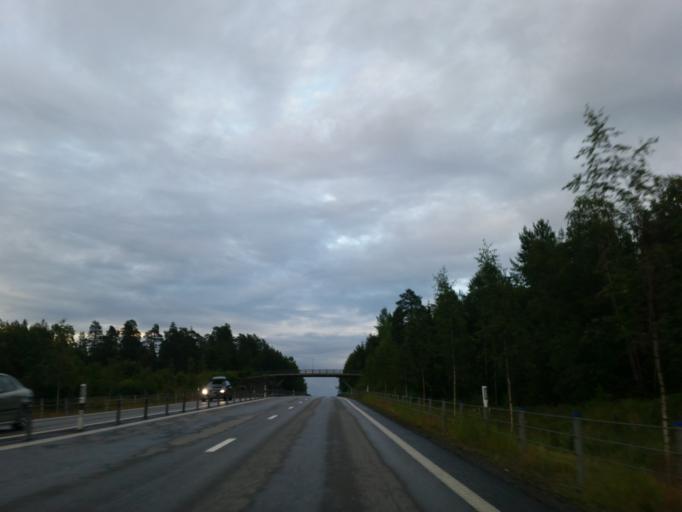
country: SE
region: Vaesterbotten
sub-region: Umea Kommun
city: Ersmark
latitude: 63.8480
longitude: 20.3232
